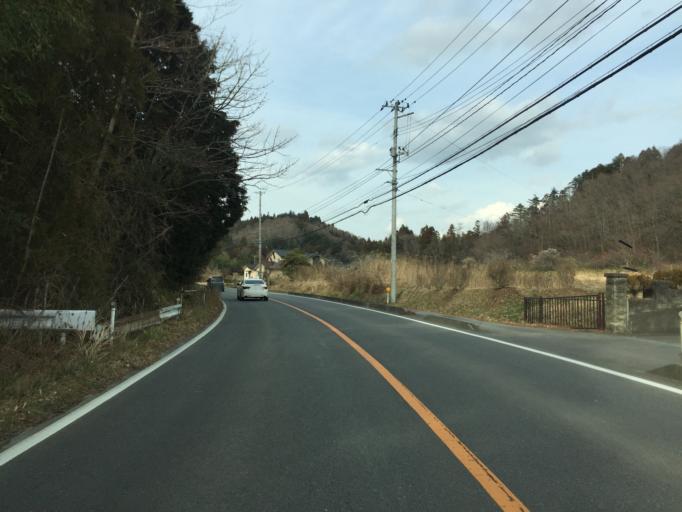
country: JP
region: Fukushima
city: Iwaki
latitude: 36.9871
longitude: 140.7377
